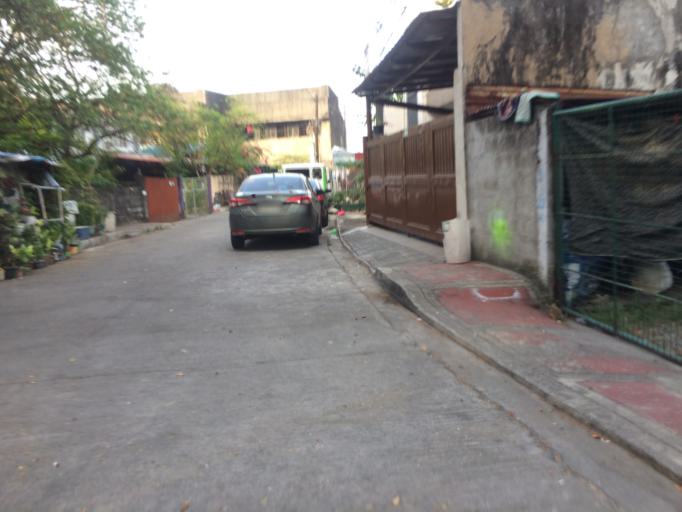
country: PH
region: Calabarzon
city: Bagong Pagasa
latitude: 14.6695
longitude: 121.0170
